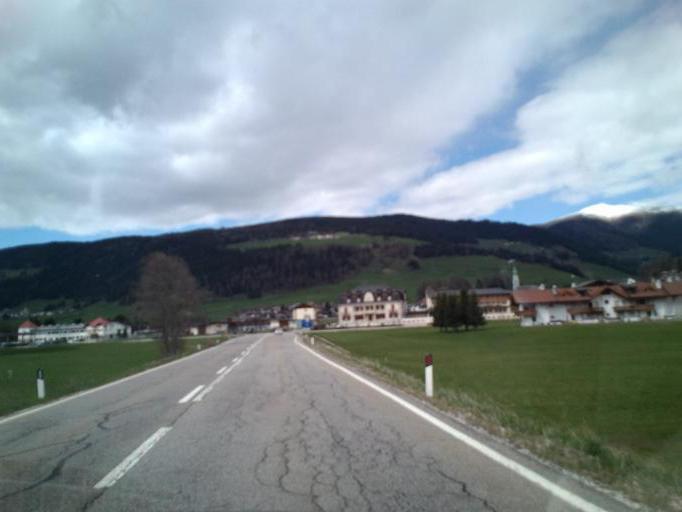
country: IT
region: Trentino-Alto Adige
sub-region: Bolzano
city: Dobbiaco
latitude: 46.7270
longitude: 12.2207
